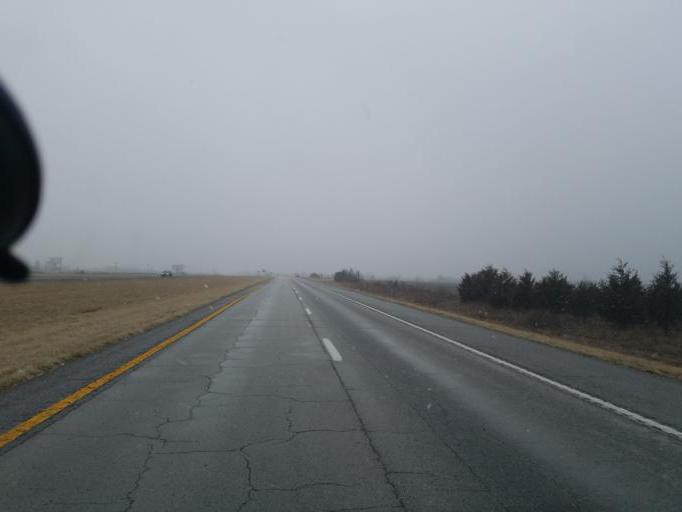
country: US
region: Missouri
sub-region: Macon County
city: La Plata
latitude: 39.9432
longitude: -92.4772
